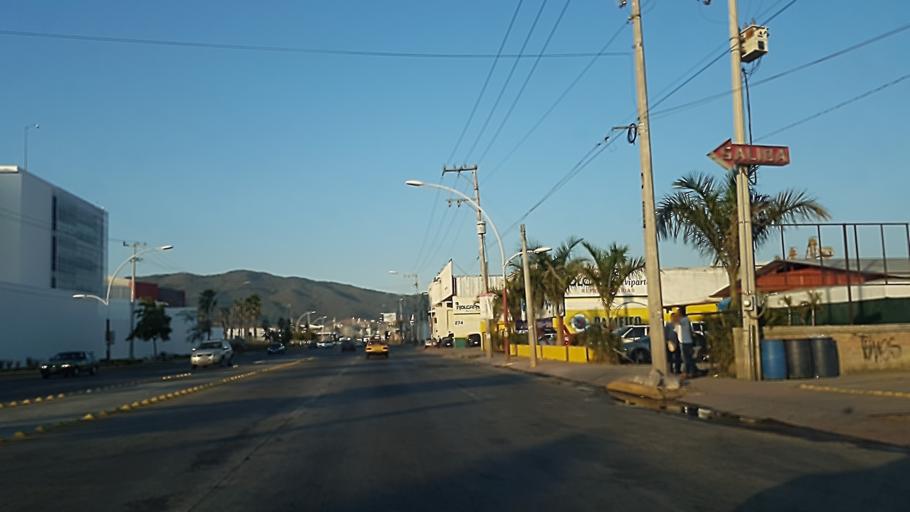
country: MX
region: Nayarit
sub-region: Tepic
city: La Corregidora
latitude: 21.4737
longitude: -104.8482
